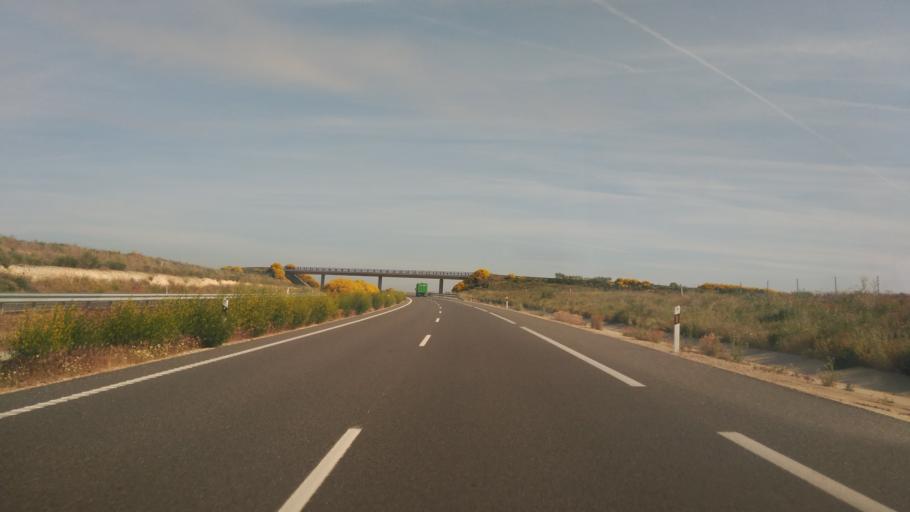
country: ES
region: Castille and Leon
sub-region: Provincia de Salamanca
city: Castellanos de Villiquera
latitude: 41.0486
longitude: -5.6687
